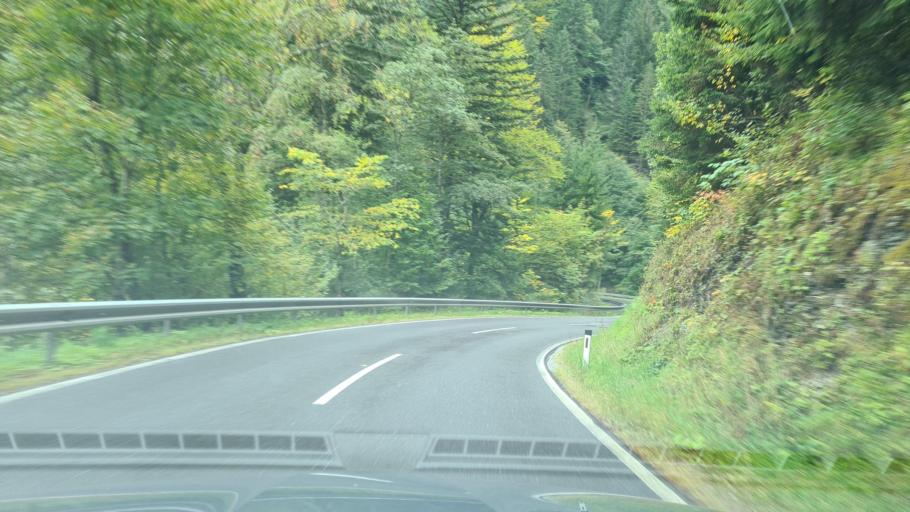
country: AT
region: Styria
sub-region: Politischer Bezirk Weiz
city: Gasen
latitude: 47.3674
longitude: 15.4859
